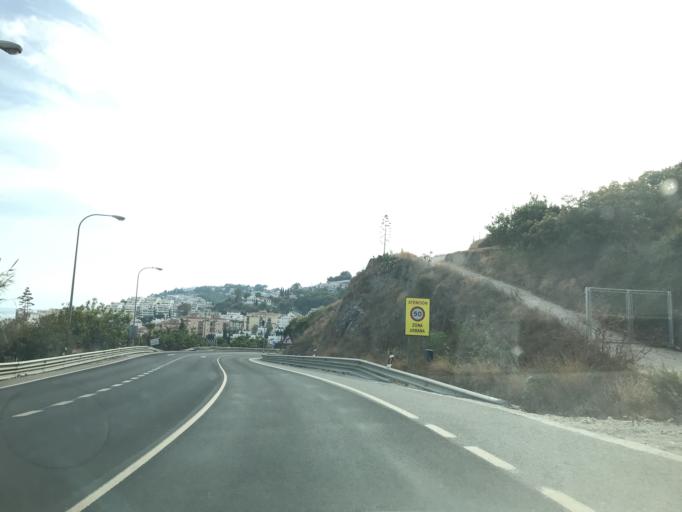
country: ES
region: Andalusia
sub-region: Provincia de Granada
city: Almunecar
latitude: 36.7497
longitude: -3.6599
